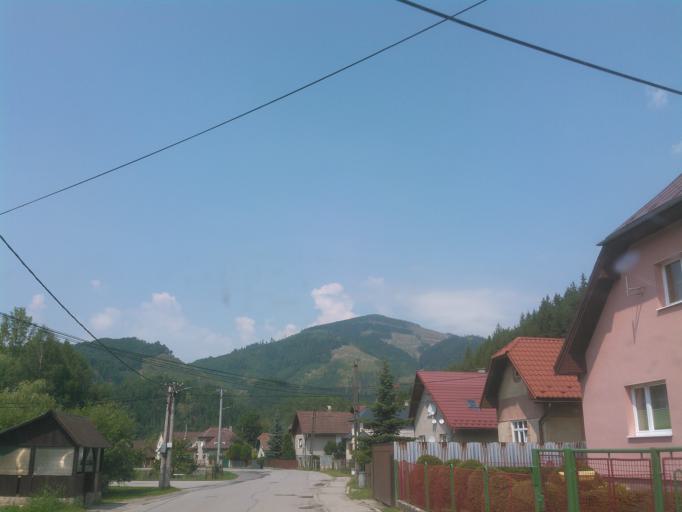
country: SK
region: Zilinsky
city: Ruzomberok
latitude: 48.9515
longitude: 19.2697
